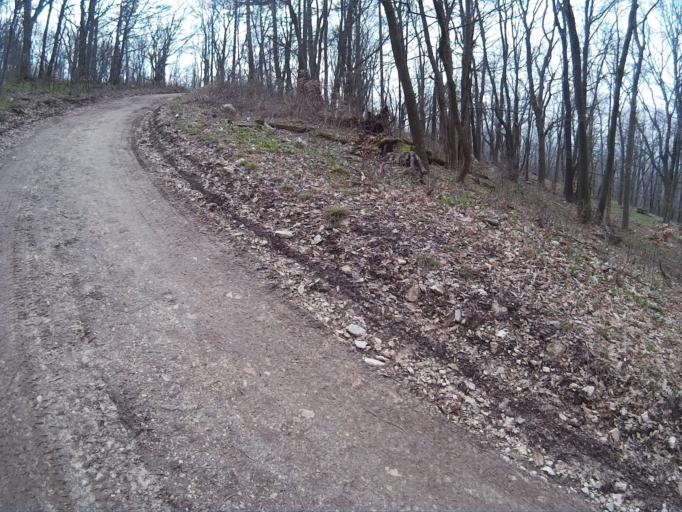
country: HU
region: Veszprem
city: Zirc
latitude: 47.1815
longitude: 17.8513
